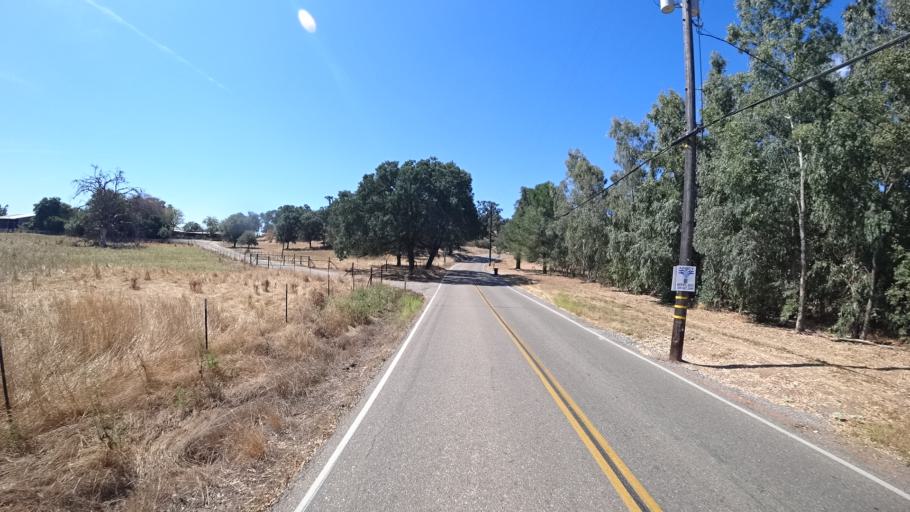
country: US
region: California
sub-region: Calaveras County
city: Rancho Calaveras
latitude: 38.1482
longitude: -120.8992
